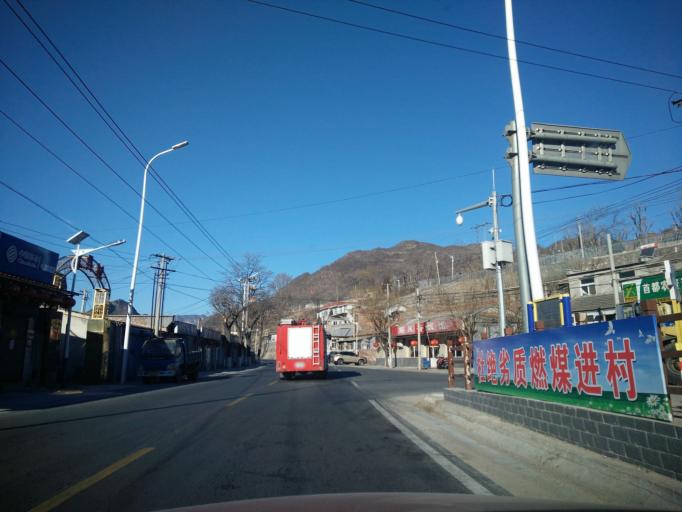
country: CN
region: Beijing
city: Yanchi
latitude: 40.0327
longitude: 115.8906
